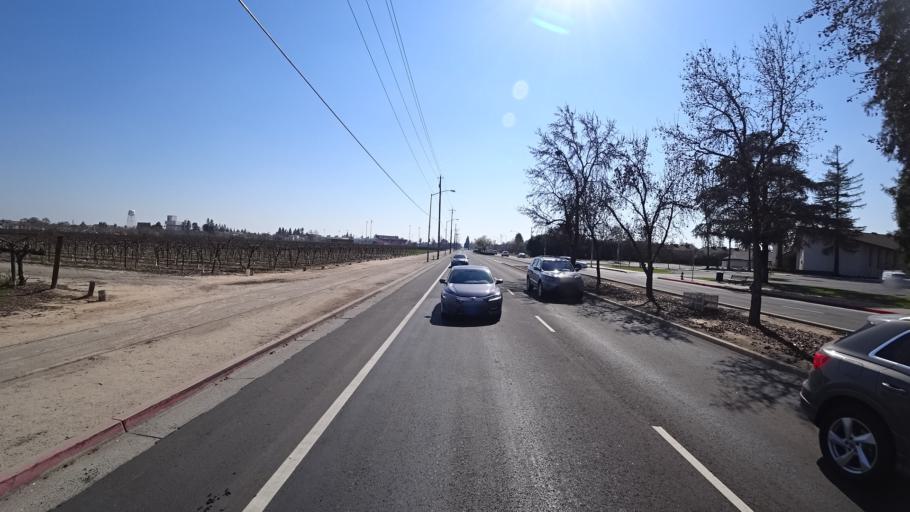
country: US
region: California
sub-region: Fresno County
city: Clovis
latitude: 36.8196
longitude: -119.7541
